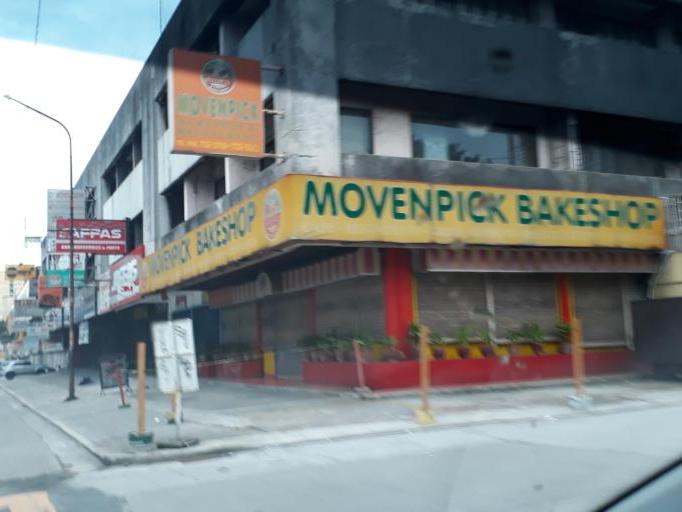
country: PH
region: Calabarzon
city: Del Monte
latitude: 14.6260
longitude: 121.0056
